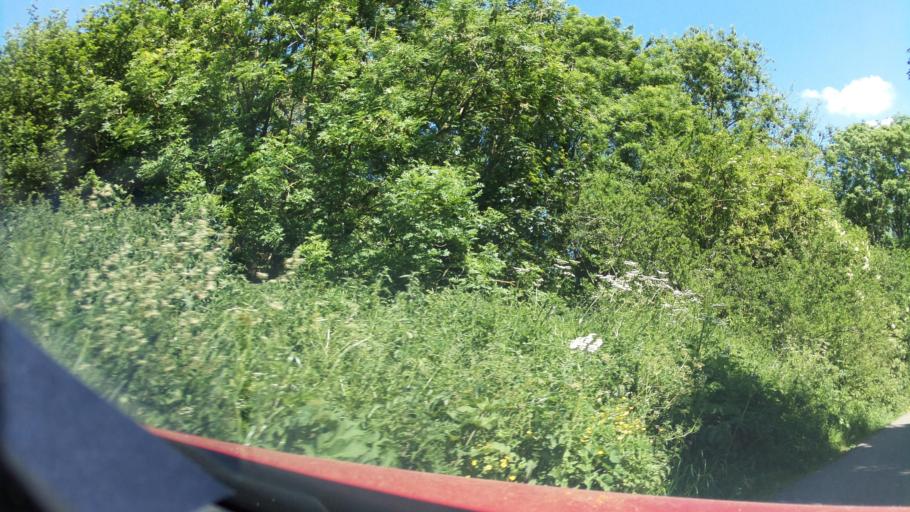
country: GB
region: England
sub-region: Wiltshire
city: Chippenham
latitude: 51.4835
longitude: -2.1161
